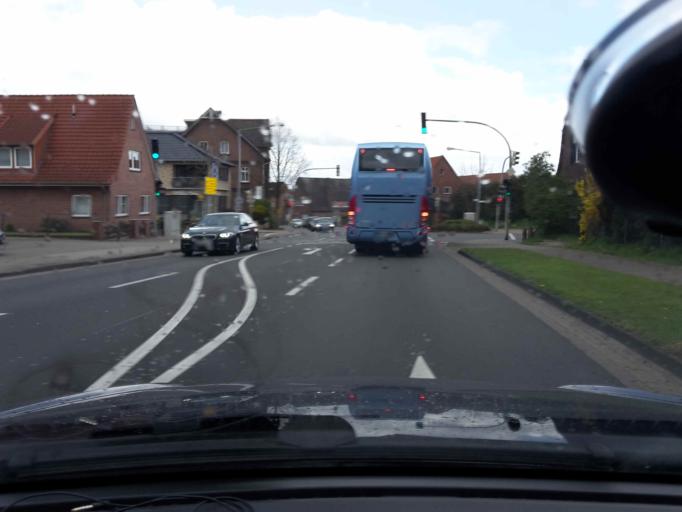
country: DE
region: Lower Saxony
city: Nottensdorf
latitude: 53.4804
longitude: 9.6363
